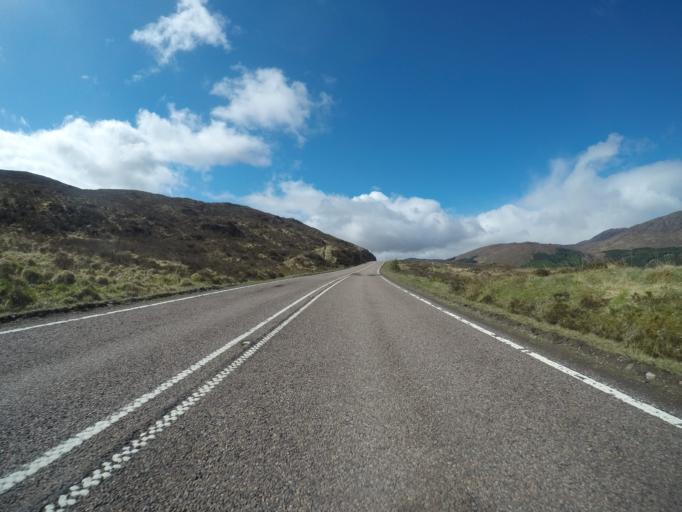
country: GB
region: Scotland
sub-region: Highland
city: Spean Bridge
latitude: 57.1211
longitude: -4.9741
